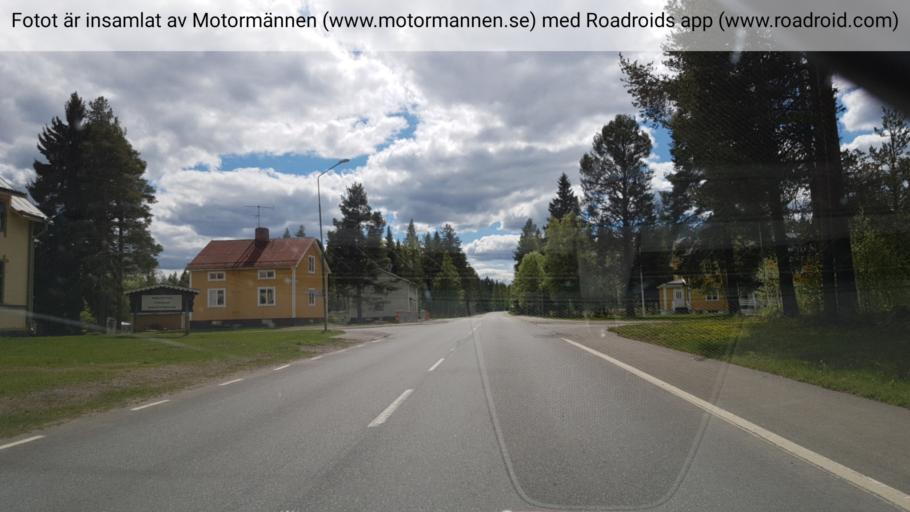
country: SE
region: Vaesterbotten
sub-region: Skelleftea Kommun
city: Langsele
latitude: 64.7923
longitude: 20.0311
